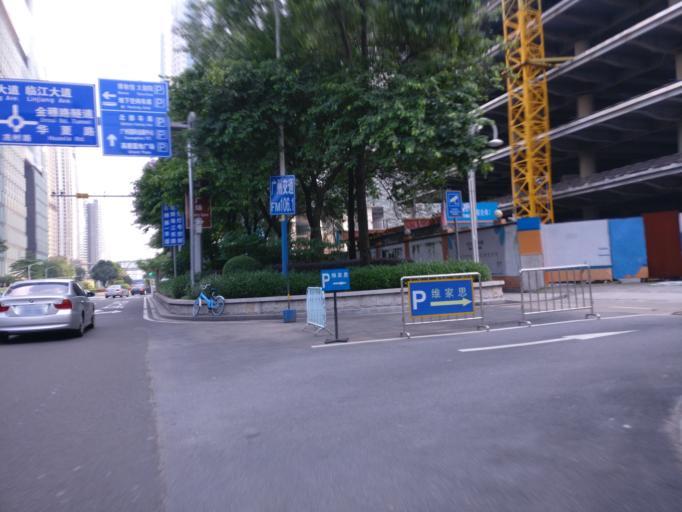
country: CN
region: Guangdong
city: Wushan
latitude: 23.1270
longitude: 113.3225
